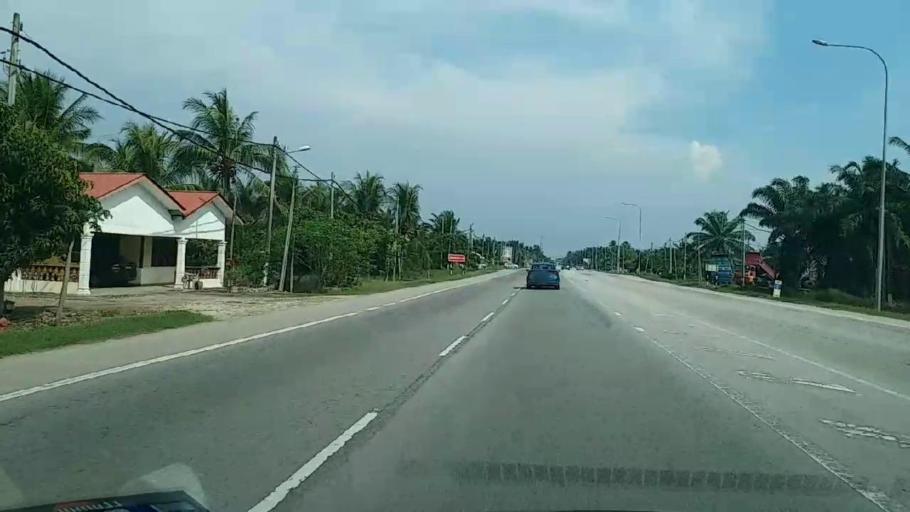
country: MY
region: Selangor
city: Kuala Selangor
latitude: 3.3741
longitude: 101.2386
